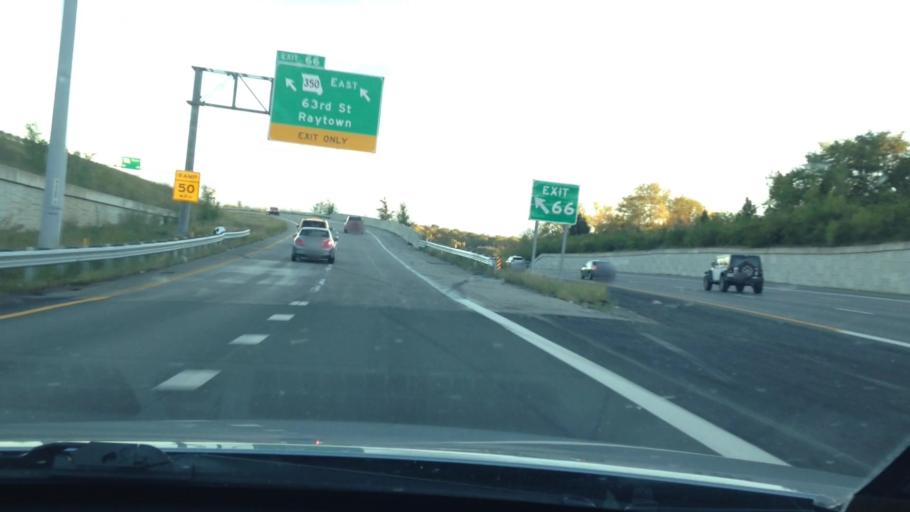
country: US
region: Missouri
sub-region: Jackson County
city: Raytown
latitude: 39.0195
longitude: -94.5009
